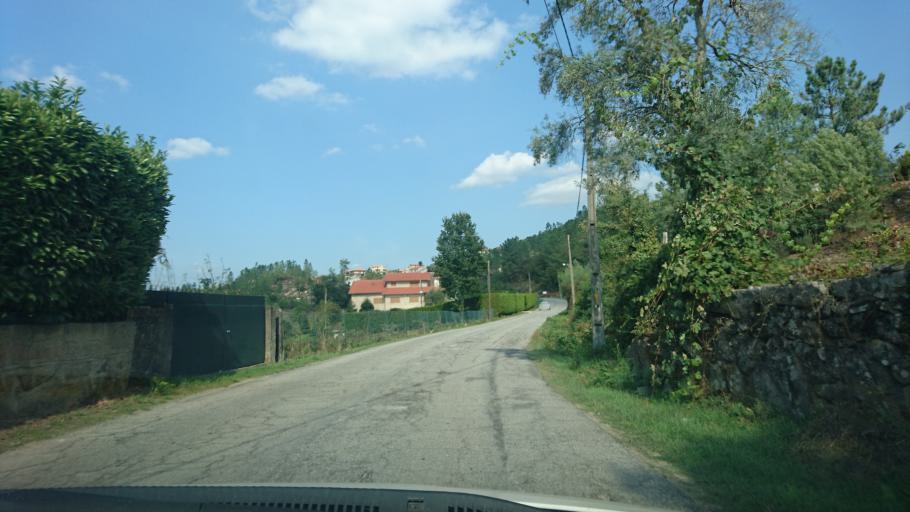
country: PT
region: Vila Real
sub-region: Mondim de Basto
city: Mondim de Basto
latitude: 41.4335
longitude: -7.9283
